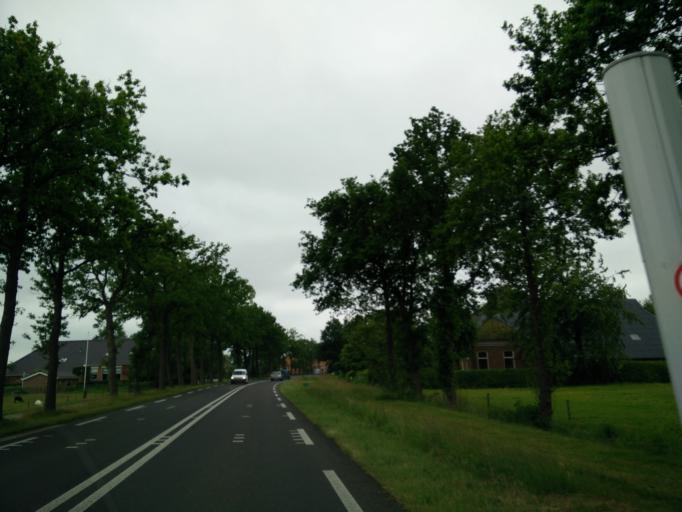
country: NL
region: Groningen
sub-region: Gemeente Groningen
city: Groningen
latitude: 53.1627
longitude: 6.4964
